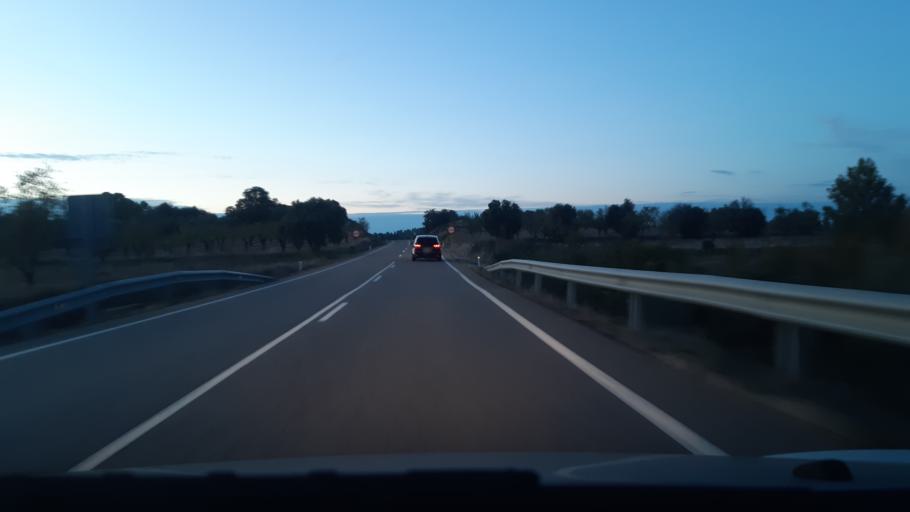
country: ES
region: Aragon
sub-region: Provincia de Teruel
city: Calaceite
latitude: 40.9715
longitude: 0.2069
